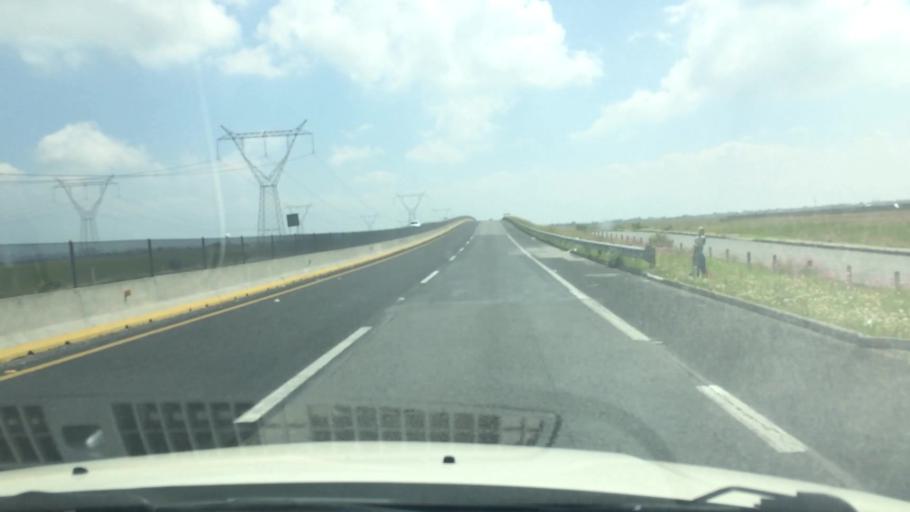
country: MX
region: Mexico
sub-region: Toluca
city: Barrio del Cajon
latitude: 19.3932
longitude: -99.6615
